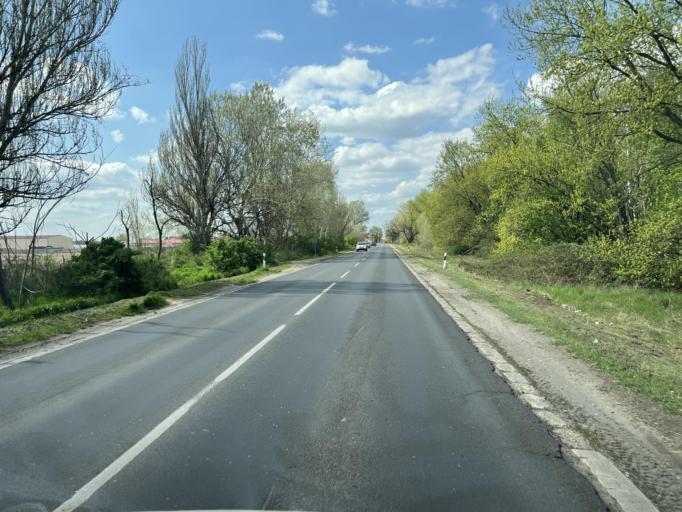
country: HU
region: Pest
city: Vecses
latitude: 47.4018
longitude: 19.2939
